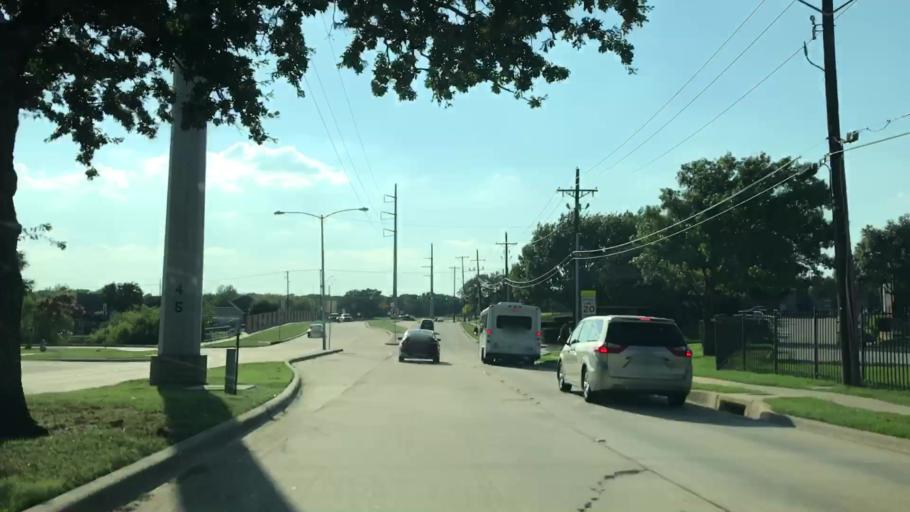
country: US
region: Texas
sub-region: Denton County
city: Lewisville
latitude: 33.0277
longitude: -97.0256
